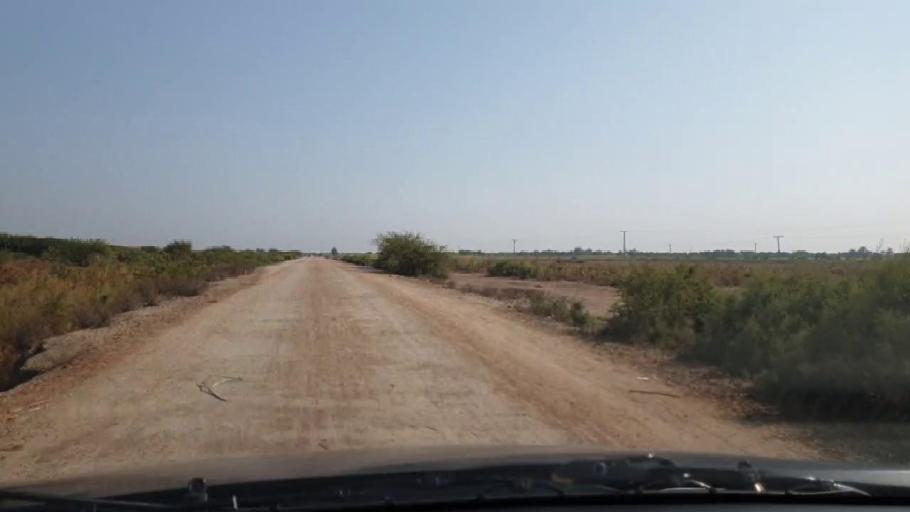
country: PK
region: Sindh
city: Jhol
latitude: 25.9962
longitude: 68.9202
